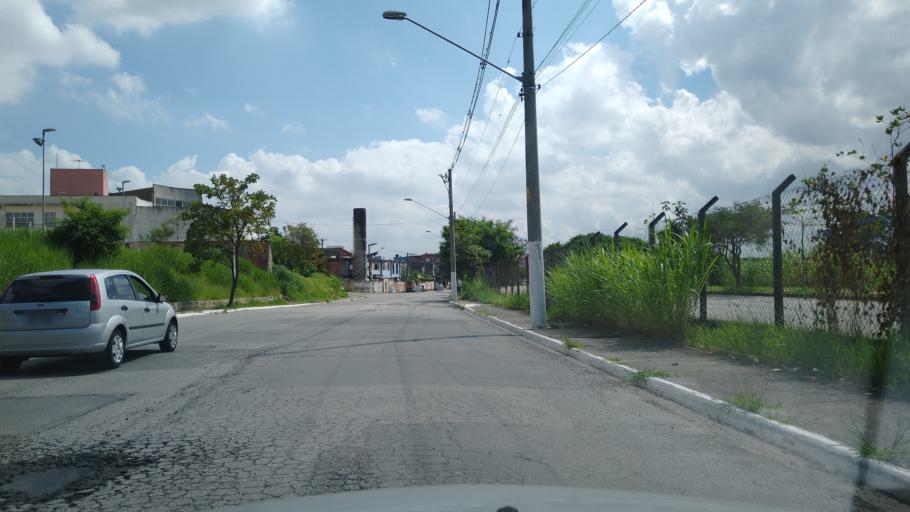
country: BR
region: Sao Paulo
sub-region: Guarulhos
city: Guarulhos
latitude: -23.4835
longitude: -46.4651
